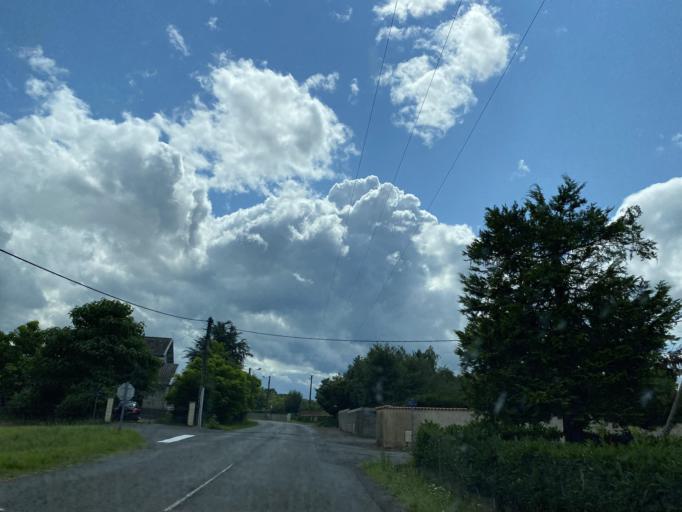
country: FR
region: Auvergne
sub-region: Departement du Puy-de-Dome
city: Peschadoires
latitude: 45.8283
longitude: 3.4870
